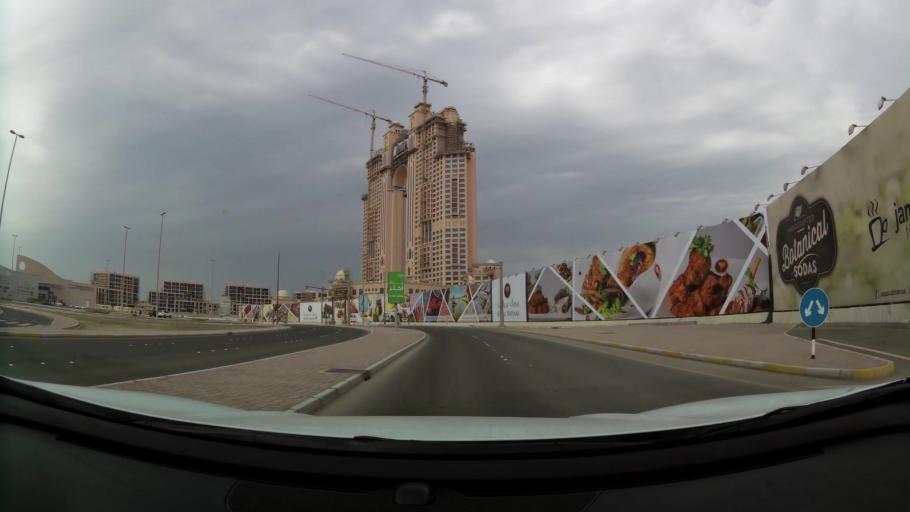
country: AE
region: Abu Dhabi
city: Abu Dhabi
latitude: 24.4785
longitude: 54.3239
